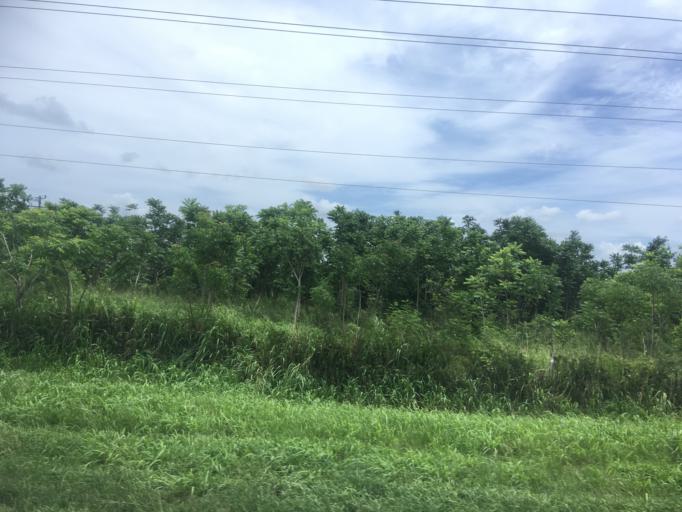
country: CU
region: Matanzas
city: Colon
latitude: 22.7042
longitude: -80.8770
